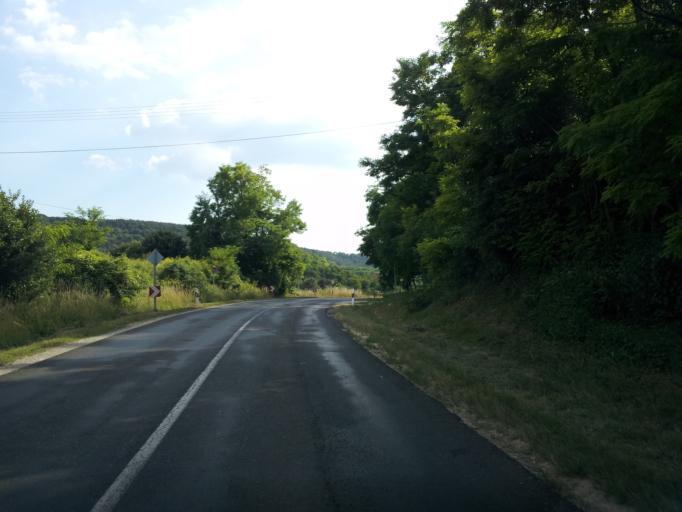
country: HU
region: Veszprem
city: Zanka
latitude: 46.9600
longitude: 17.6205
